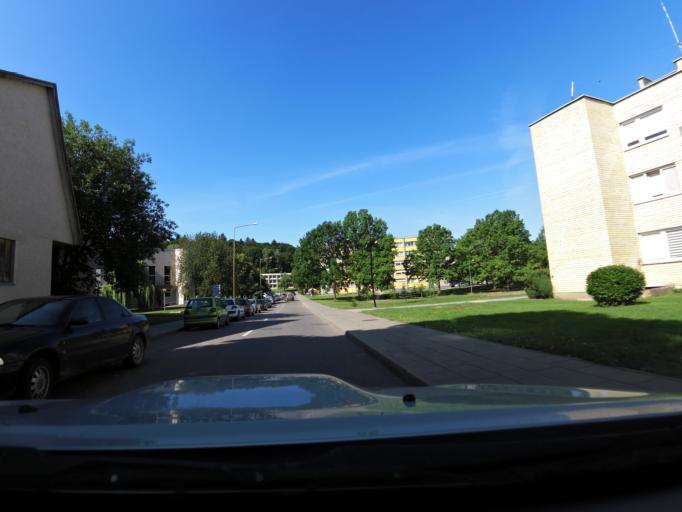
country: LT
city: Birstonas
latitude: 54.6027
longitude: 24.0310
